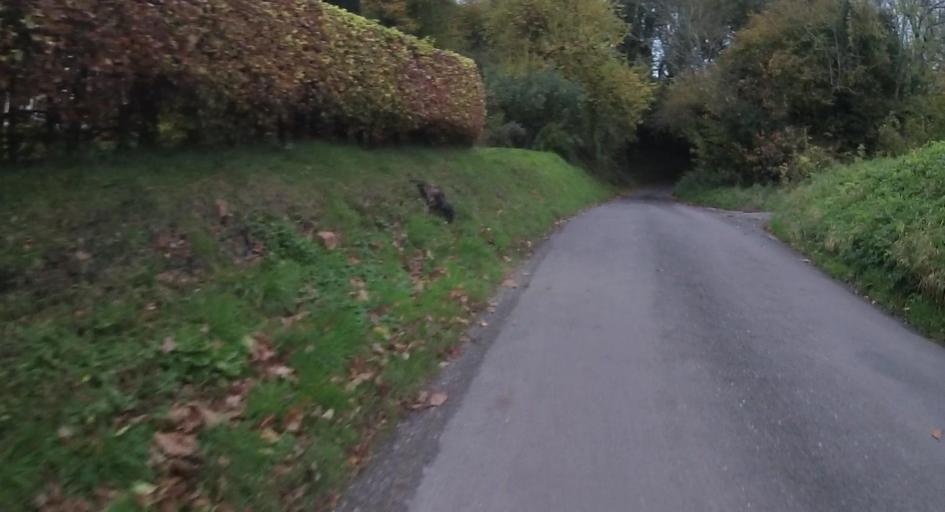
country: GB
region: England
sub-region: Hampshire
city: Kingsley
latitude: 51.1512
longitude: -0.8813
